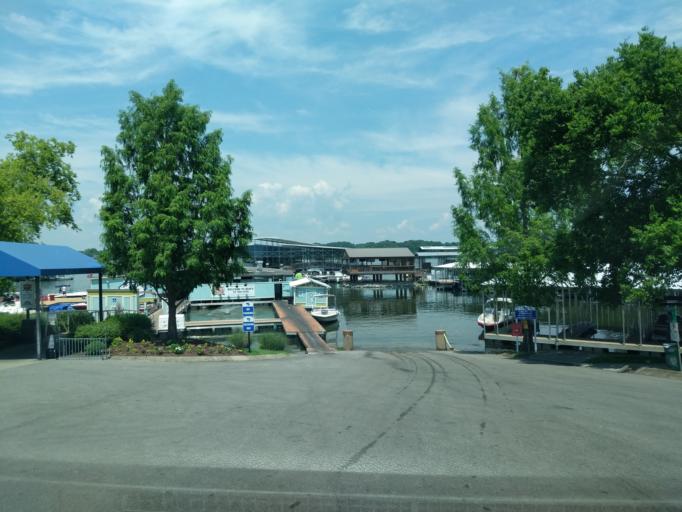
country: US
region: Tennessee
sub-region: Davidson County
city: Lakewood
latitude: 36.2513
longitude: -86.6396
